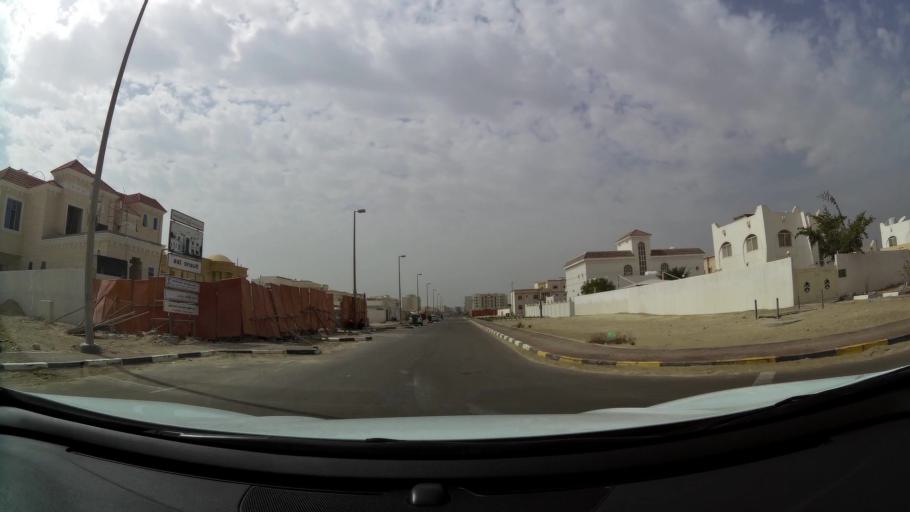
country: AE
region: Abu Dhabi
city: Abu Dhabi
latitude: 24.3178
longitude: 54.6257
